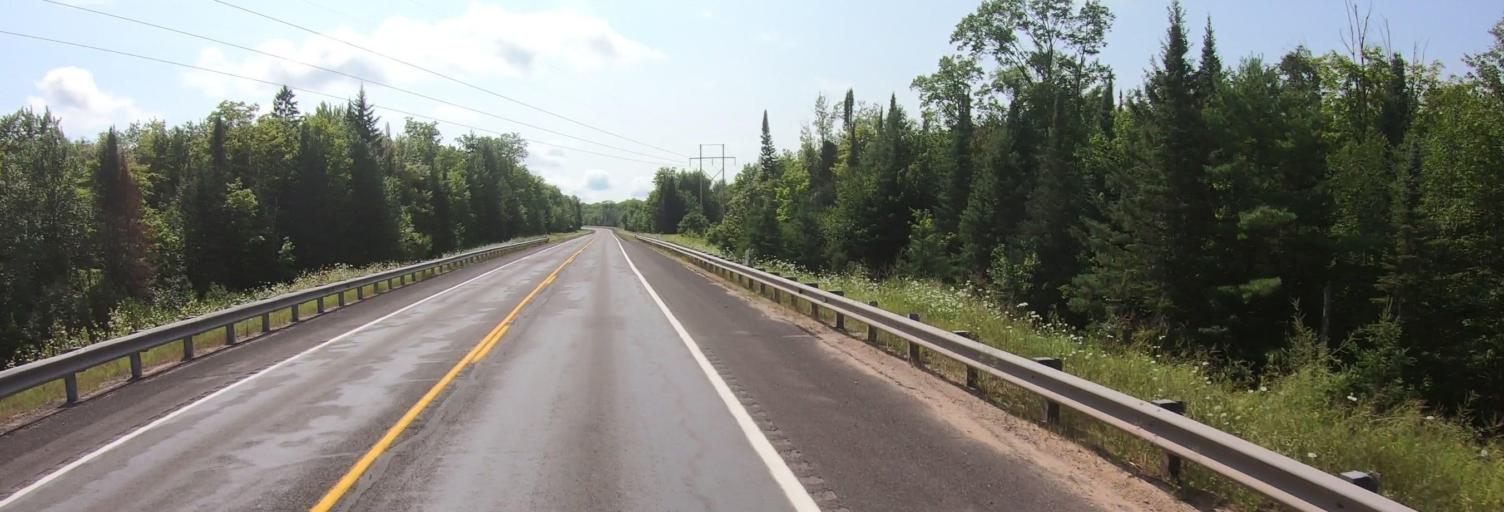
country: US
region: Michigan
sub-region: Ontonagon County
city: Ontonagon
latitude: 46.8520
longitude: -88.9662
